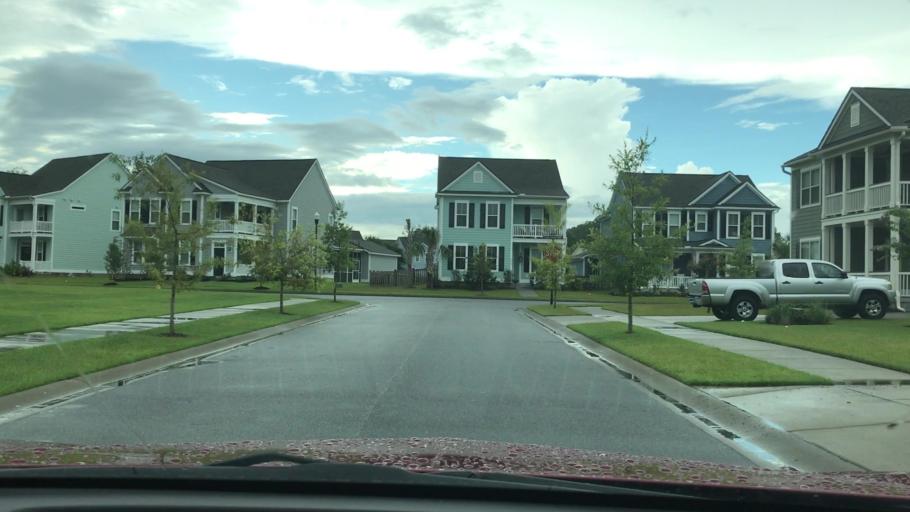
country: US
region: South Carolina
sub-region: Charleston County
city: Shell Point
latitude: 32.8072
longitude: -80.0701
